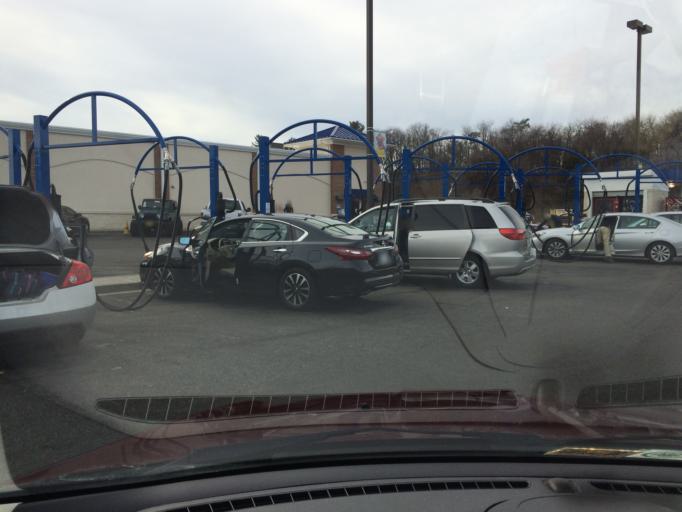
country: US
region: Virginia
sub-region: Roanoke County
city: Vinton
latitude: 37.3139
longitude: -79.8813
